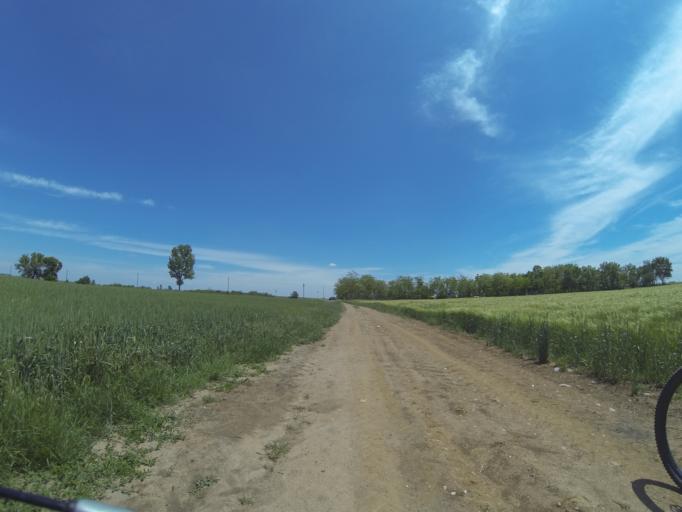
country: RO
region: Dolj
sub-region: Comuna Diosti
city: Radomir
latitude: 44.1461
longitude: 24.1626
